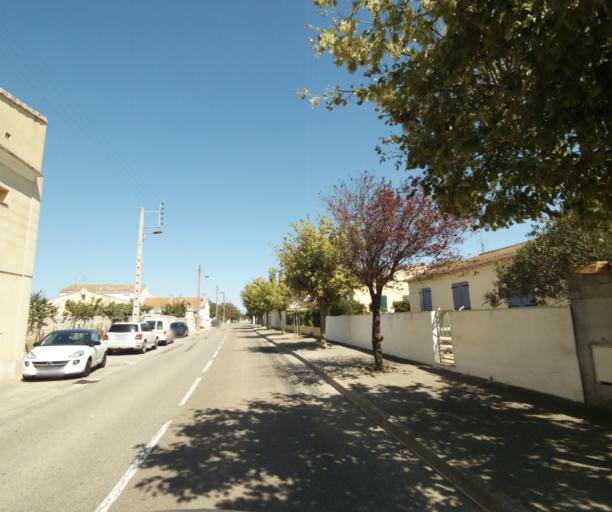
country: FR
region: Languedoc-Roussillon
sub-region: Departement du Gard
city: Rodilhan
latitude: 43.8288
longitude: 4.4308
